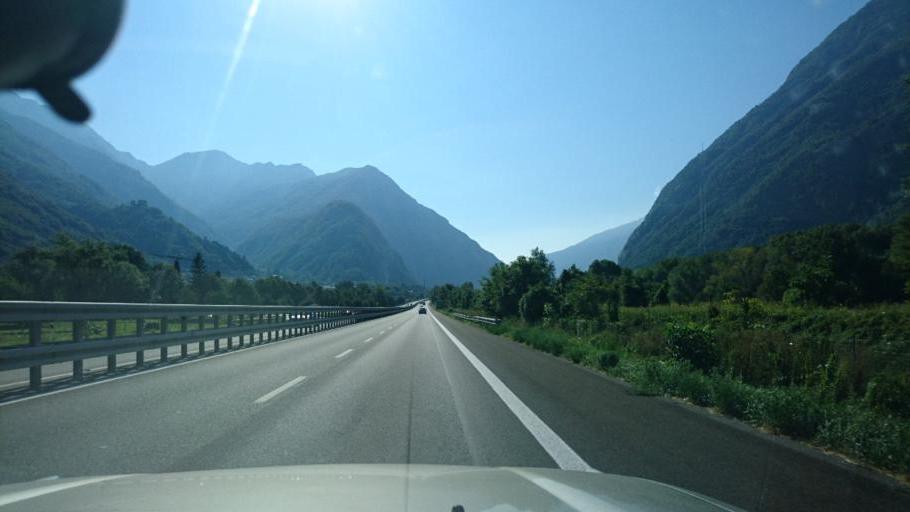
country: IT
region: Aosta Valley
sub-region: Valle d'Aosta
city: Arnad
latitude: 45.6465
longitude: 7.7110
